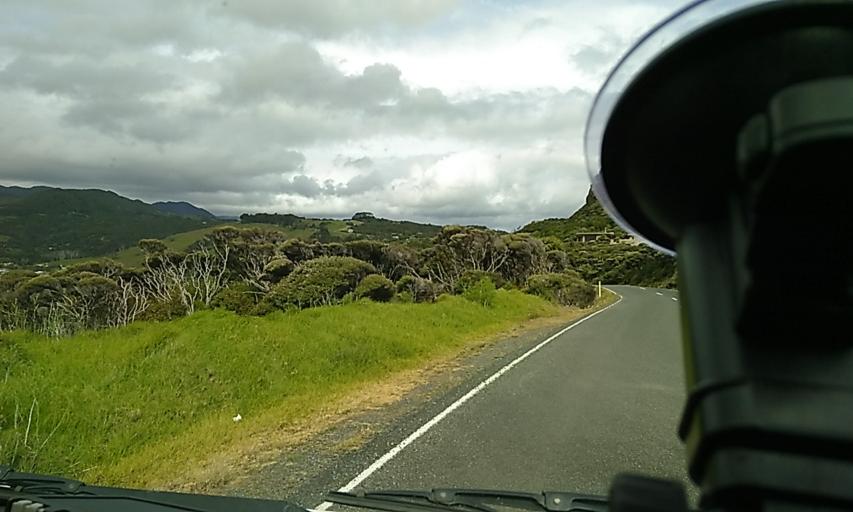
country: NZ
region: Northland
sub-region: Far North District
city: Ahipara
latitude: -35.5383
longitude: 173.3732
